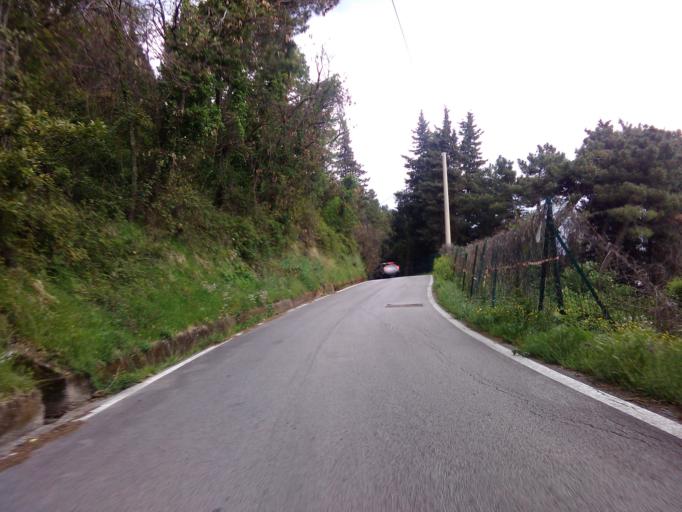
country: IT
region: Tuscany
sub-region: Provincia di Lucca
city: Pontestazzemese
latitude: 43.9566
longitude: 10.2771
